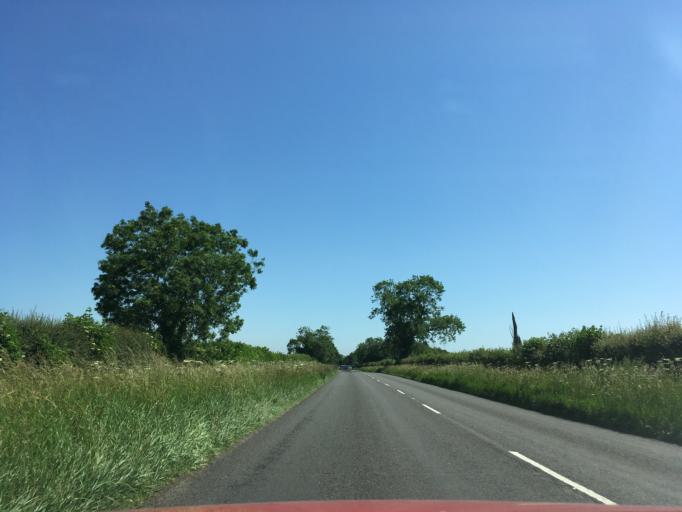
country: GB
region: England
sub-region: Oxfordshire
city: Hook Norton
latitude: 51.9628
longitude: -1.4946
